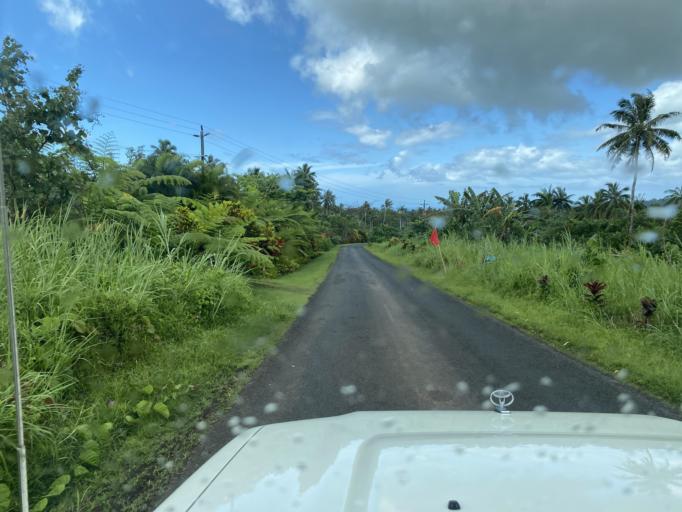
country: WS
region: Va`a-o-Fonoti
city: Samamea
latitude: -13.9753
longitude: -171.5840
